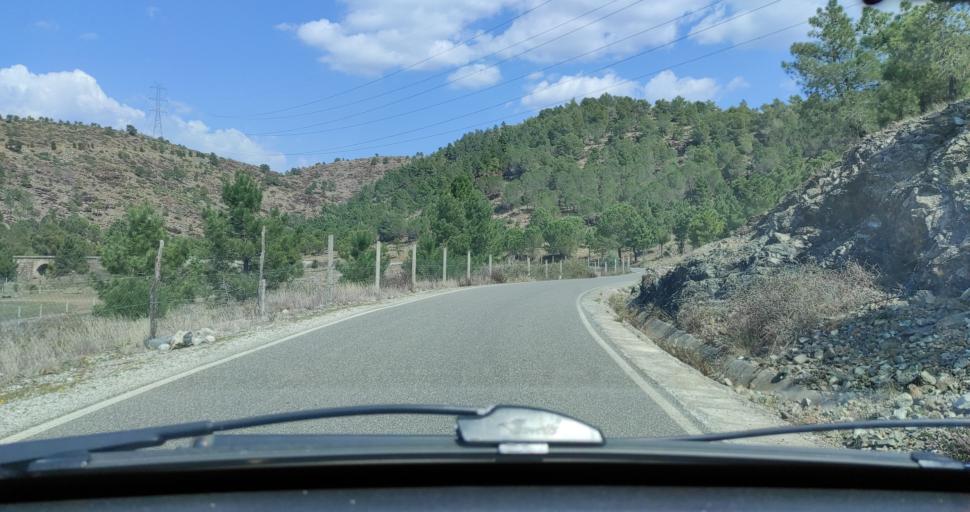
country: AL
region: Shkoder
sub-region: Rrethi i Shkodres
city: Hajmel
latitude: 41.9804
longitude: 19.6457
